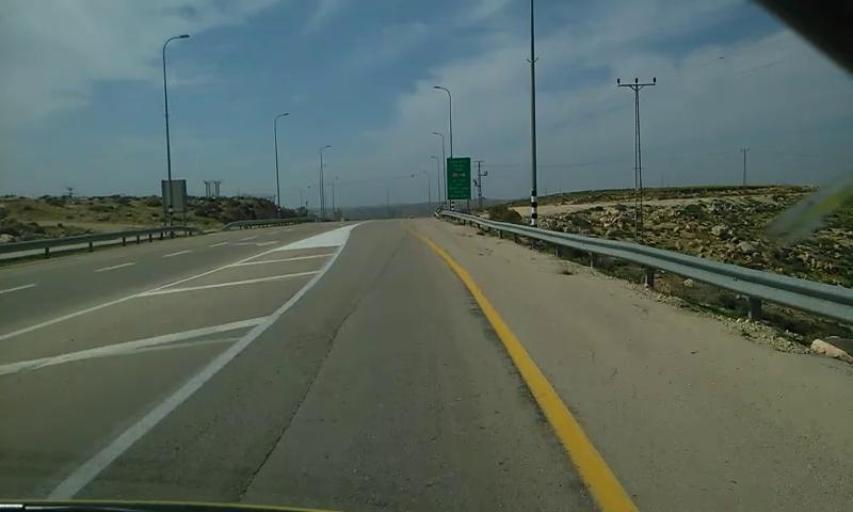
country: PS
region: West Bank
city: Az Zahiriyah
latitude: 31.3766
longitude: 35.0054
